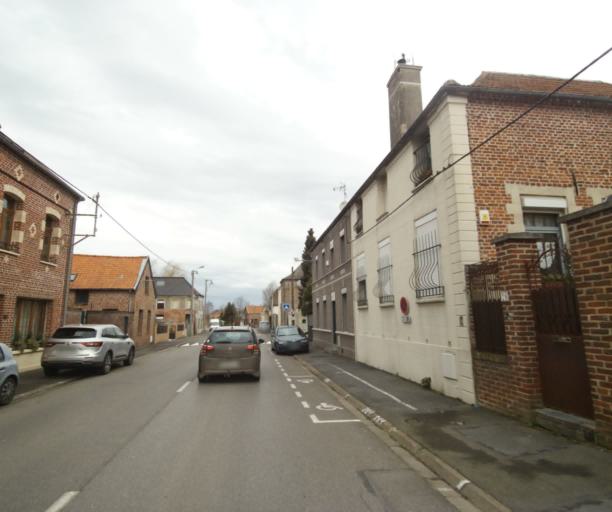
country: FR
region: Nord-Pas-de-Calais
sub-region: Departement du Nord
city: Curgies
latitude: 50.3311
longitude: 3.5996
